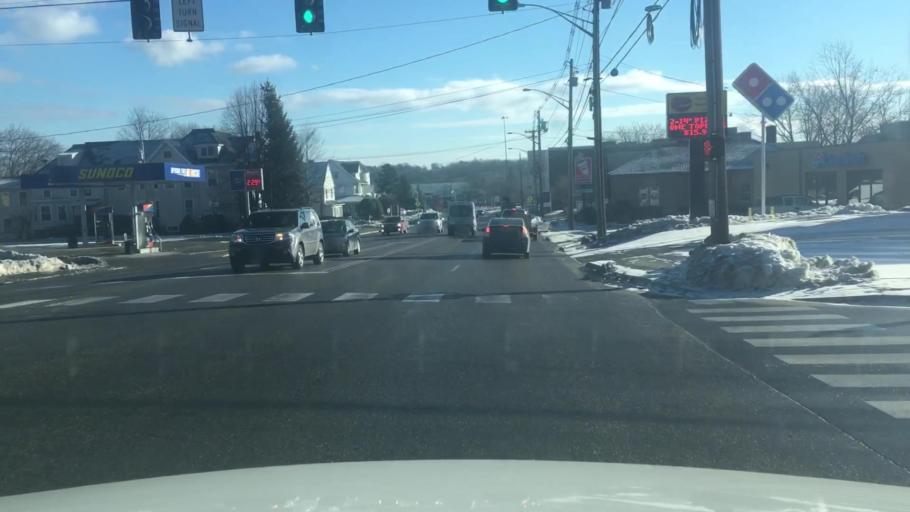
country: US
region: Maine
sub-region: Kennebec County
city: Augusta
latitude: 44.3111
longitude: -69.7831
